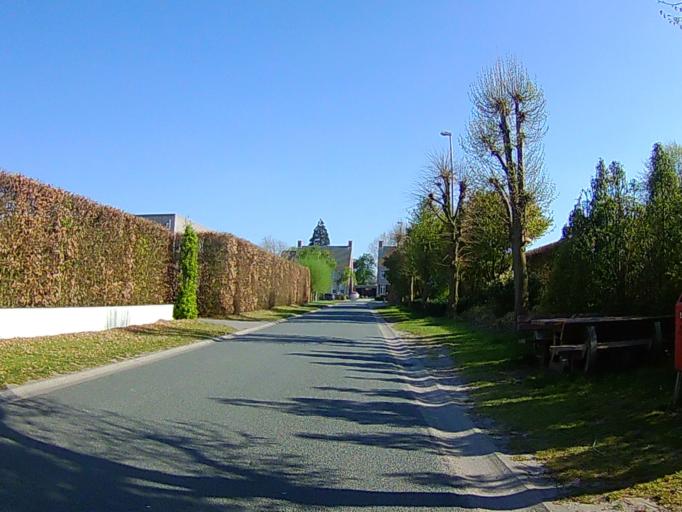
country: BE
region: Flanders
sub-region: Provincie Antwerpen
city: Hoogstraten
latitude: 51.4003
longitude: 4.7681
